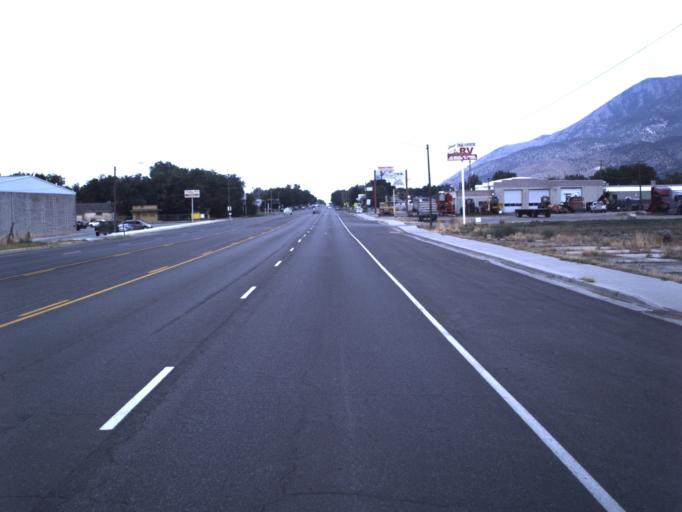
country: US
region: Utah
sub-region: Juab County
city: Nephi
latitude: 39.6946
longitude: -111.8360
